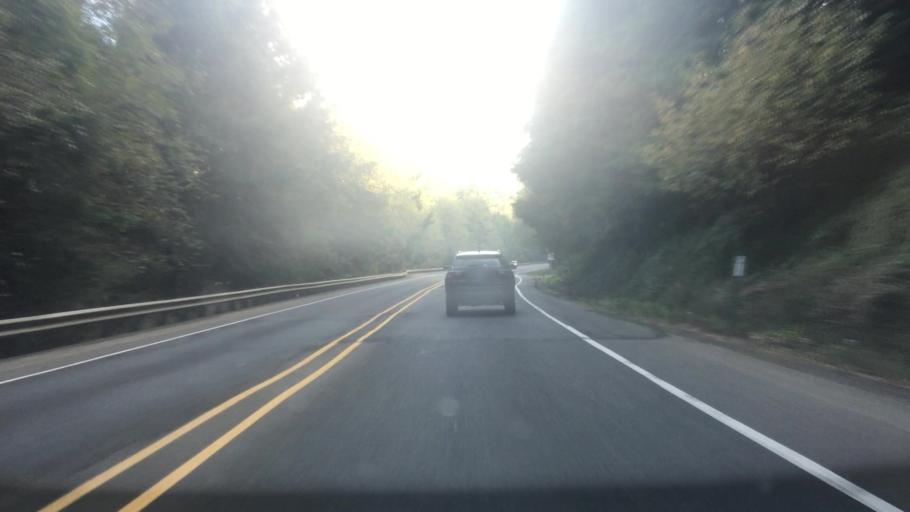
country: US
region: Oregon
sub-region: Clatsop County
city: Cannon Beach
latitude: 45.9271
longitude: -123.9295
